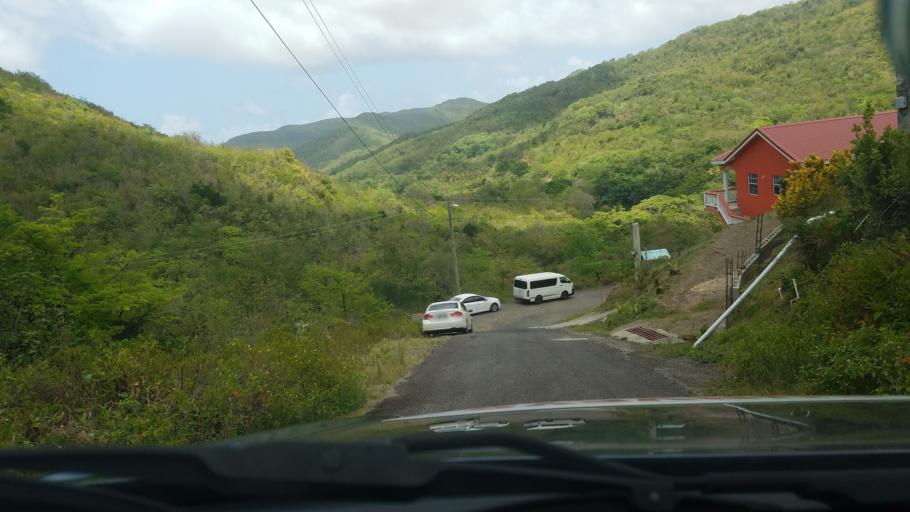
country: LC
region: Gros-Islet
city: Gros Islet
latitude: 14.0582
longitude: -60.9299
